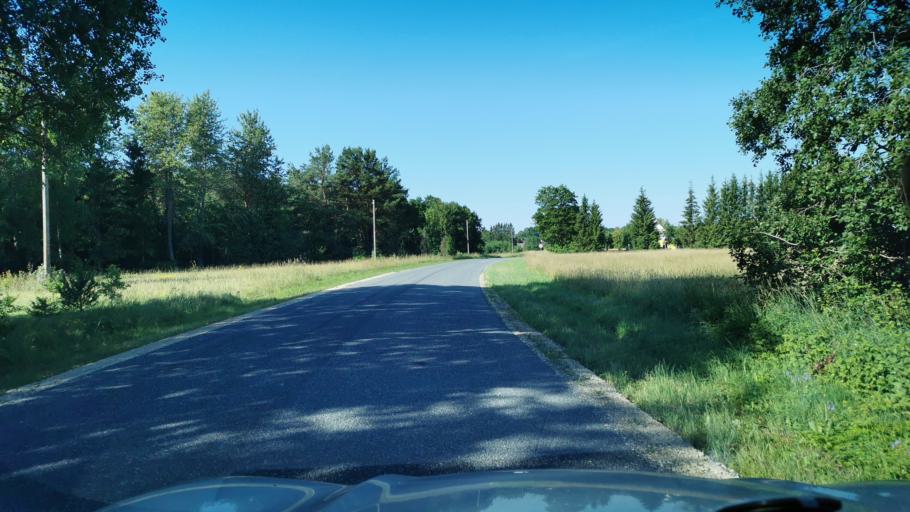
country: EE
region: Harju
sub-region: Paldiski linn
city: Paldiski
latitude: 59.2113
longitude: 24.0219
